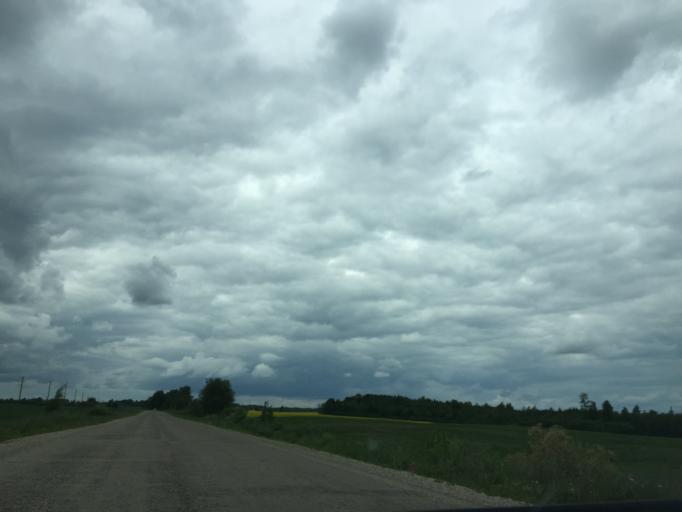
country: LV
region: Dagda
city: Dagda
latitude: 56.0379
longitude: 27.5896
